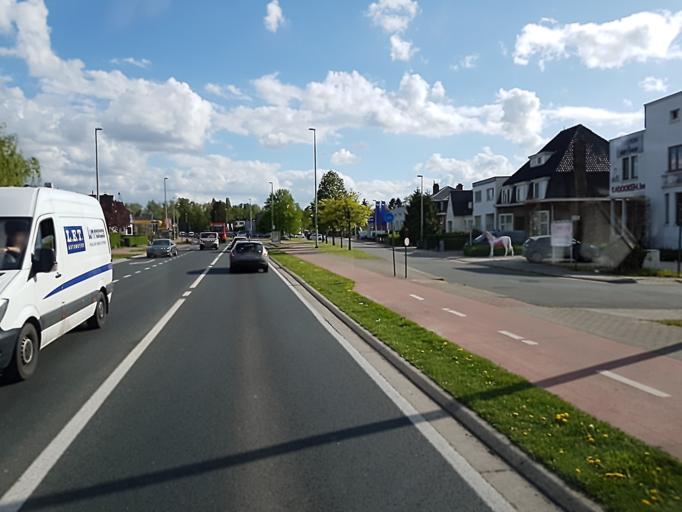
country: BE
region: Flanders
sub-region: Provincie Oost-Vlaanderen
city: Dendermonde
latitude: 51.0405
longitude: 4.1023
